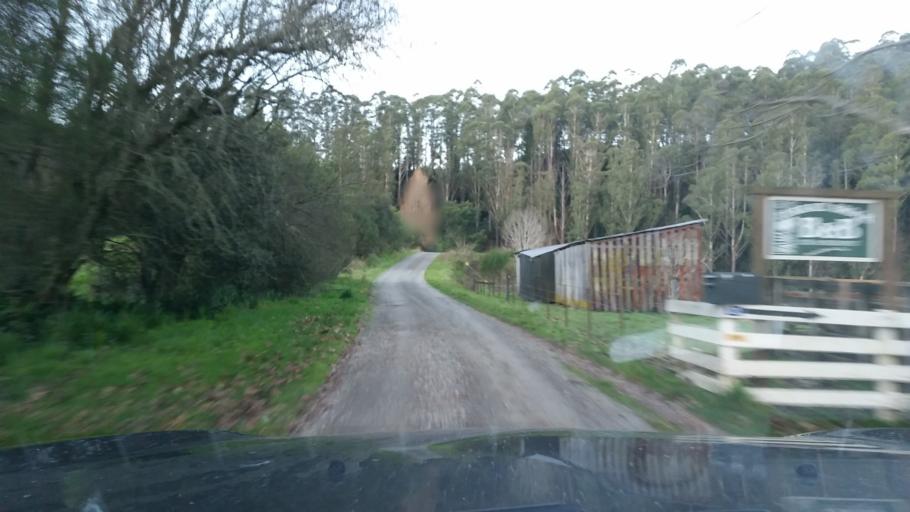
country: NZ
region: Marlborough
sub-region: Marlborough District
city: Blenheim
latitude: -41.4729
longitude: 173.7434
